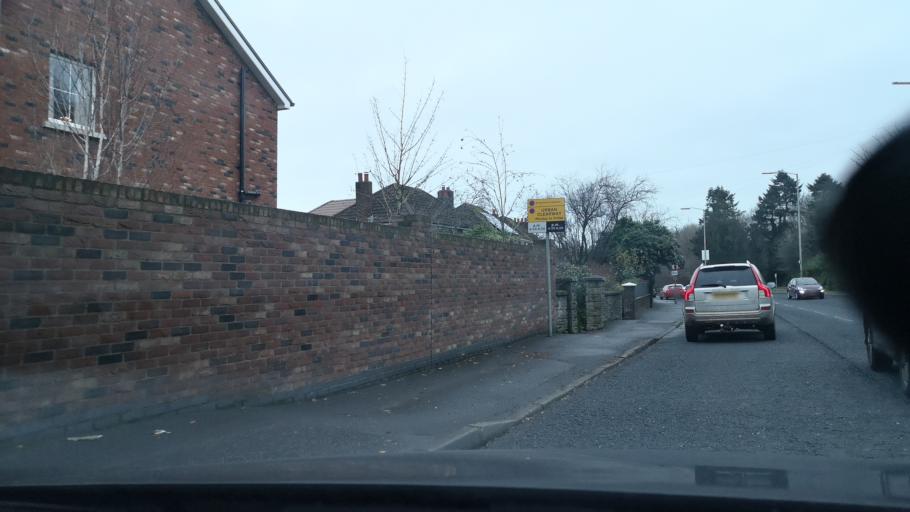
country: GB
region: Northern Ireland
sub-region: Castlereagh District
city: Castlereagh
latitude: 54.5883
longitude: -5.8566
